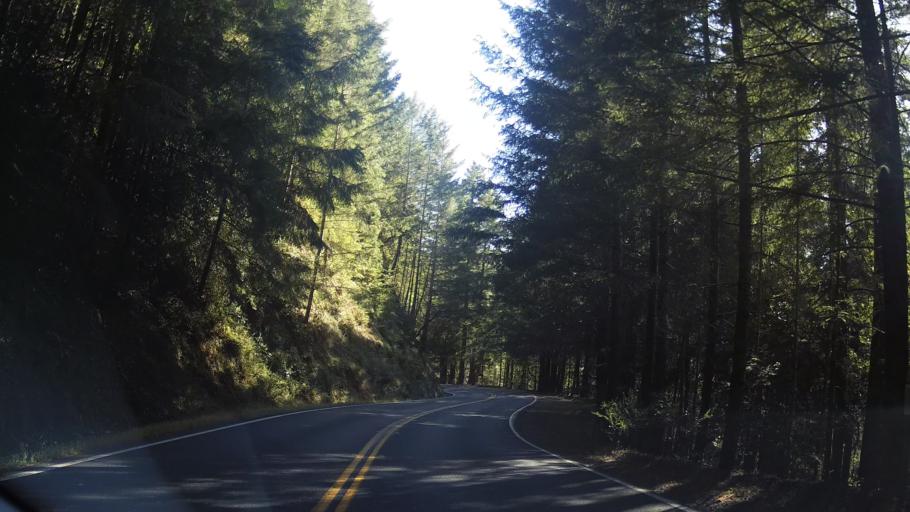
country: US
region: California
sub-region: Mendocino County
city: Brooktrails
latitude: 39.3659
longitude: -123.5004
